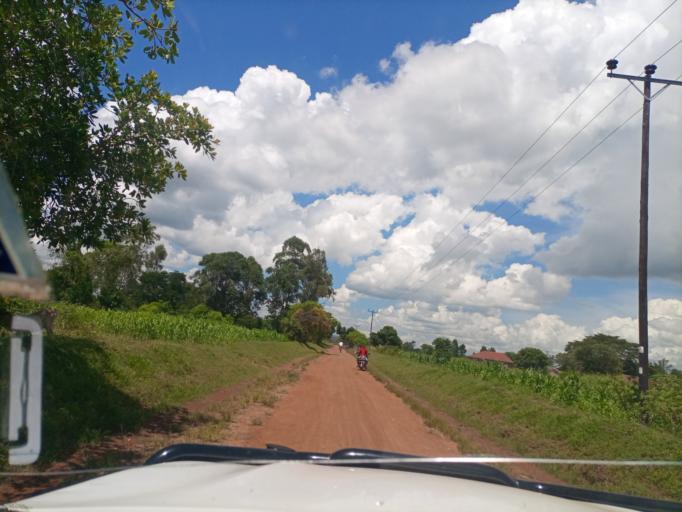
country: UG
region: Eastern Region
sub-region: Tororo District
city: Tororo
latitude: 0.6495
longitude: 33.9969
